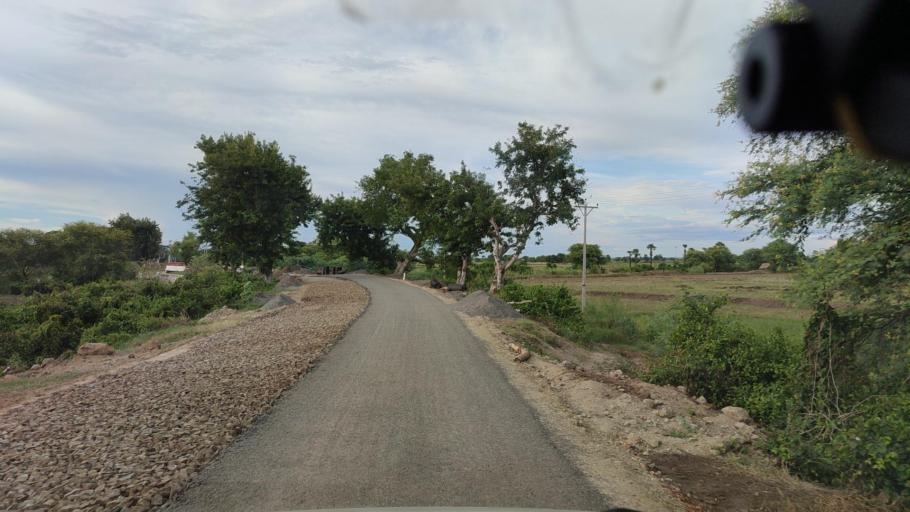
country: MM
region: Magway
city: Minbu
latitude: 20.3122
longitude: 94.7572
